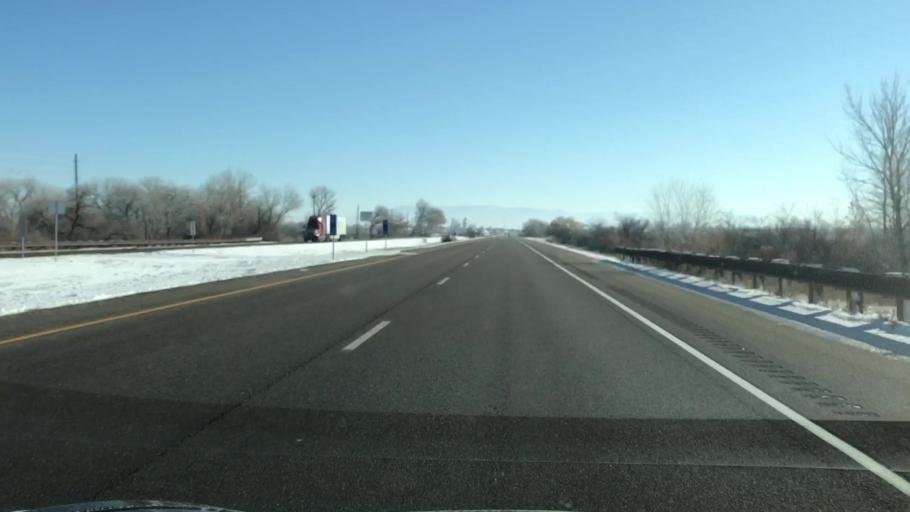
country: US
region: Colorado
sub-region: Mesa County
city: Fruita
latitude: 39.1595
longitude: -108.7575
